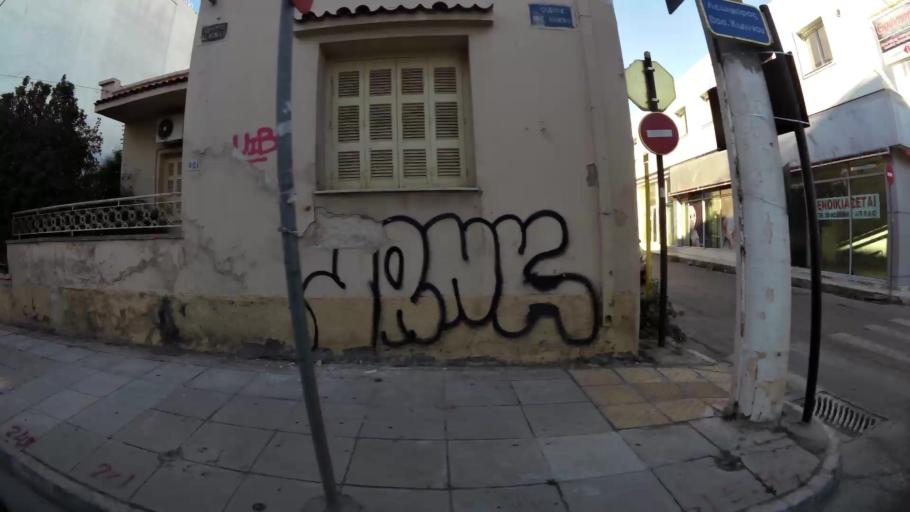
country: GR
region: Attica
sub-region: Nomarchia Anatolikis Attikis
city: Koropi
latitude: 37.9087
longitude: 23.8734
